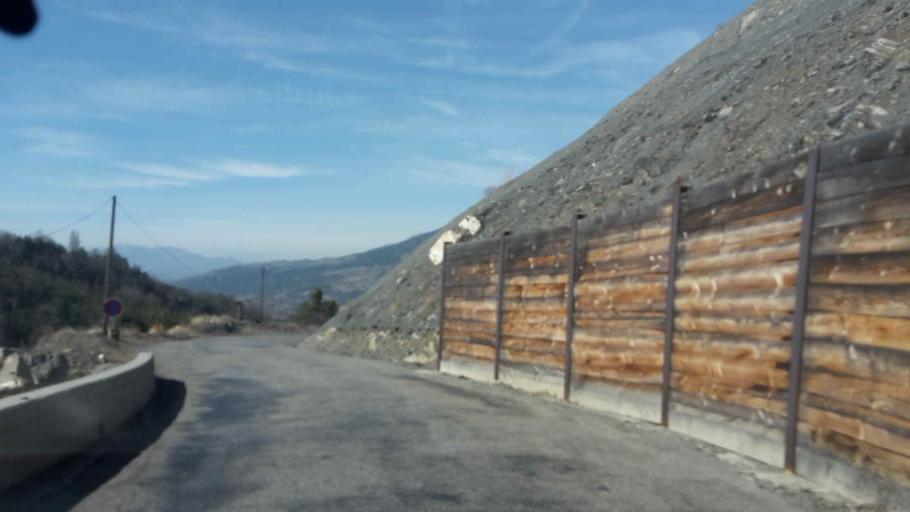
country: FR
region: Provence-Alpes-Cote d'Azur
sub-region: Departement des Hautes-Alpes
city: Embrun
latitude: 44.5624
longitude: 6.5515
